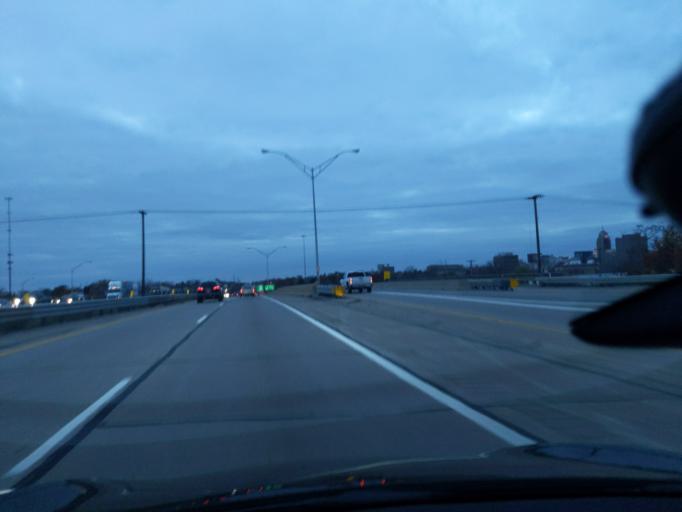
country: US
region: Michigan
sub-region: Ingham County
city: Lansing
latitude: 42.7257
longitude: -84.5403
